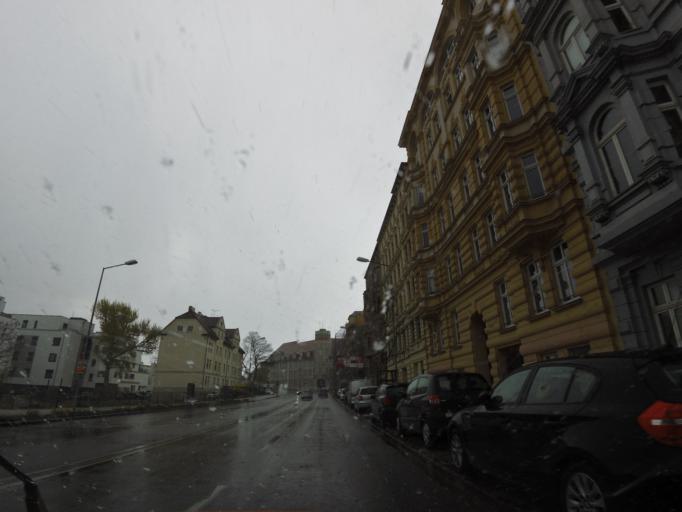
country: DE
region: Saxony-Anhalt
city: Magdeburg
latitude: 52.1191
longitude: 11.6314
